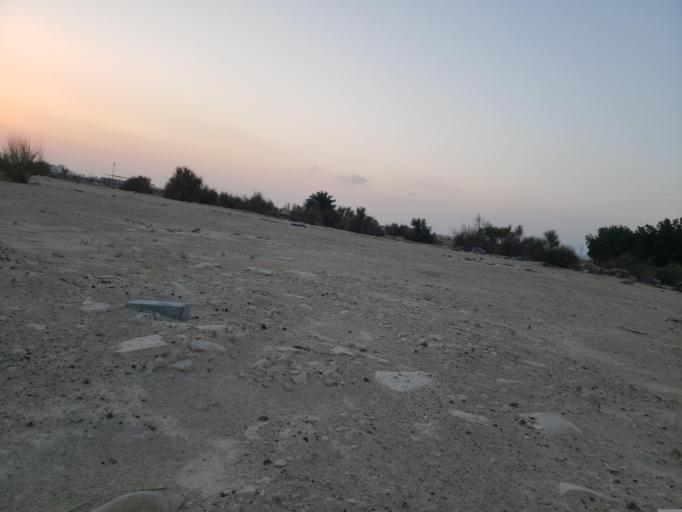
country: AE
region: Dubai
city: Dubai
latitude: 25.0018
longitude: 55.2479
